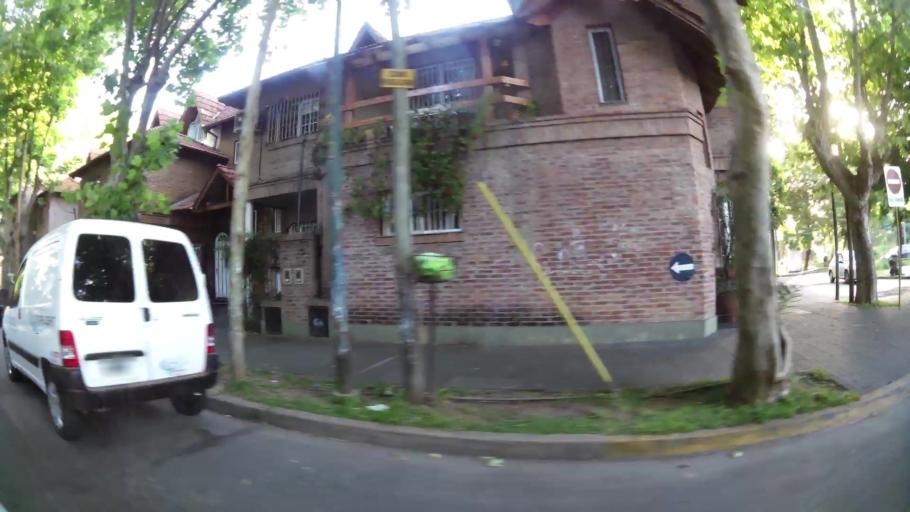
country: AR
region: Buenos Aires
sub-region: Partido de General San Martin
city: General San Martin
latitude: -34.5690
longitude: -58.5359
